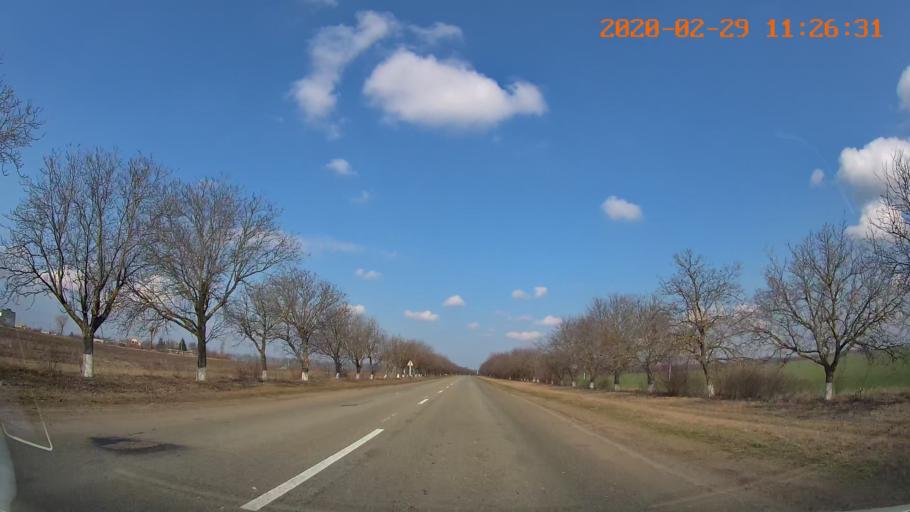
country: MD
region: Telenesti
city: Cocieri
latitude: 47.4543
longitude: 29.1457
